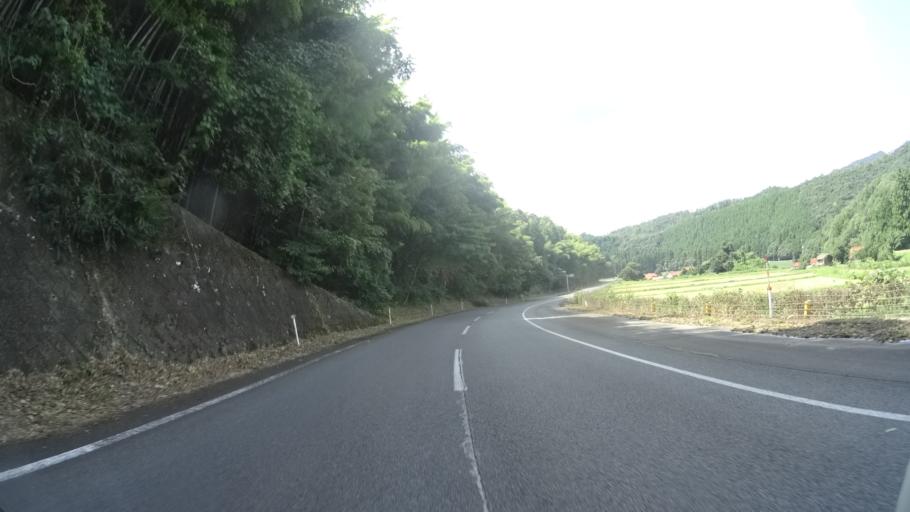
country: JP
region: Yamaguchi
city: Hagi
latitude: 34.4910
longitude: 131.5538
